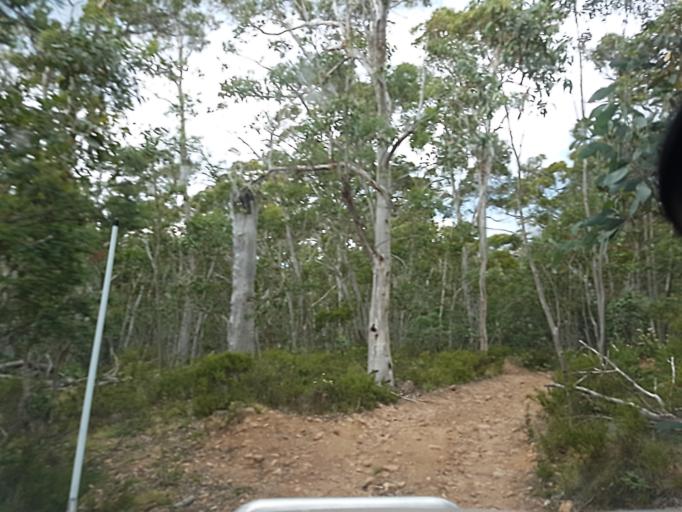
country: AU
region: New South Wales
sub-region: Snowy River
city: Jindabyne
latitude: -36.8767
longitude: 148.1616
